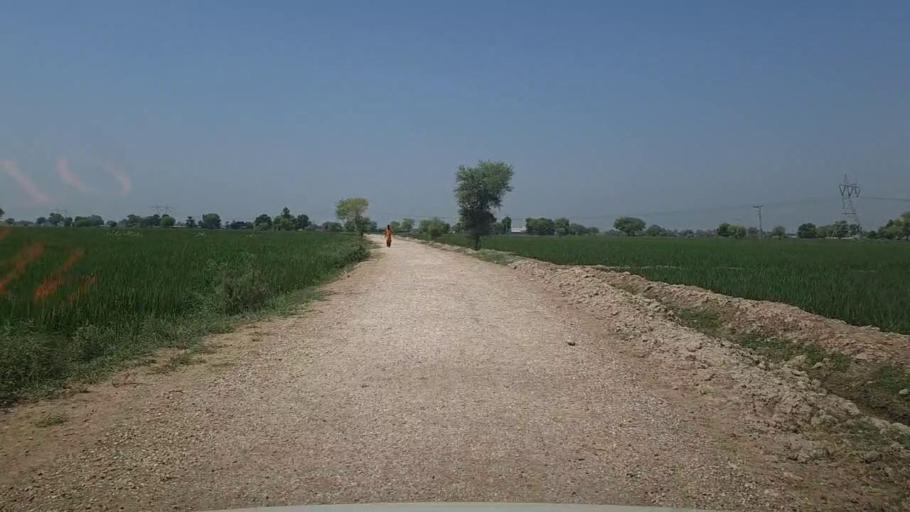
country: PK
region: Sindh
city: Kandhkot
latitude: 28.3192
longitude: 69.3807
